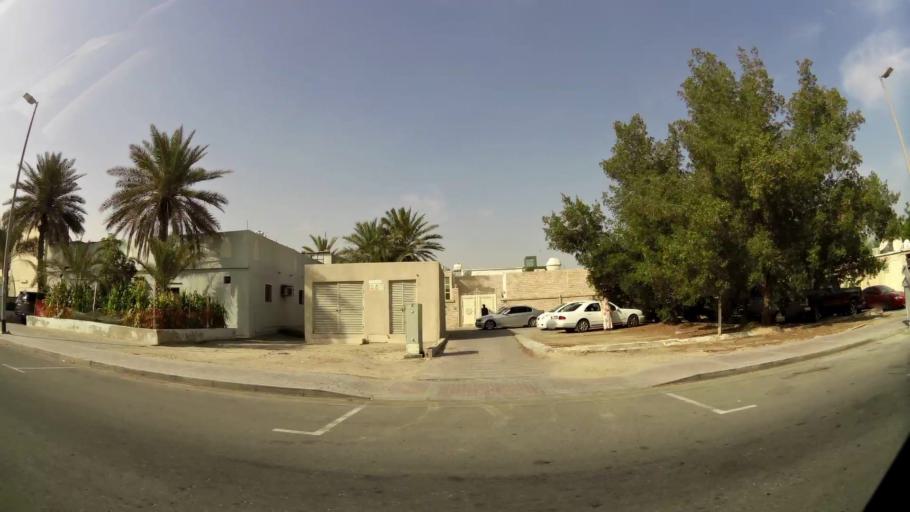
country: AE
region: Ash Shariqah
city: Sharjah
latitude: 25.2224
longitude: 55.3850
